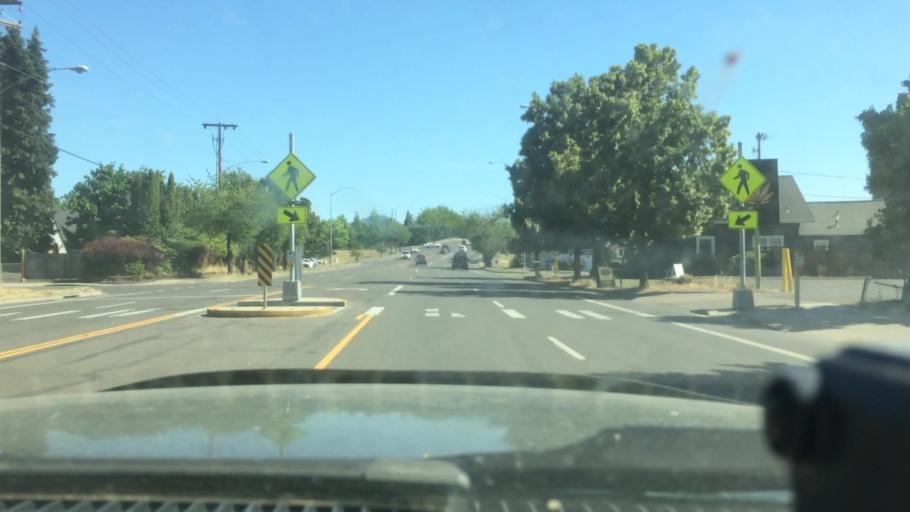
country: US
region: Oregon
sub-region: Lane County
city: Eugene
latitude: 44.0662
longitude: -123.1176
